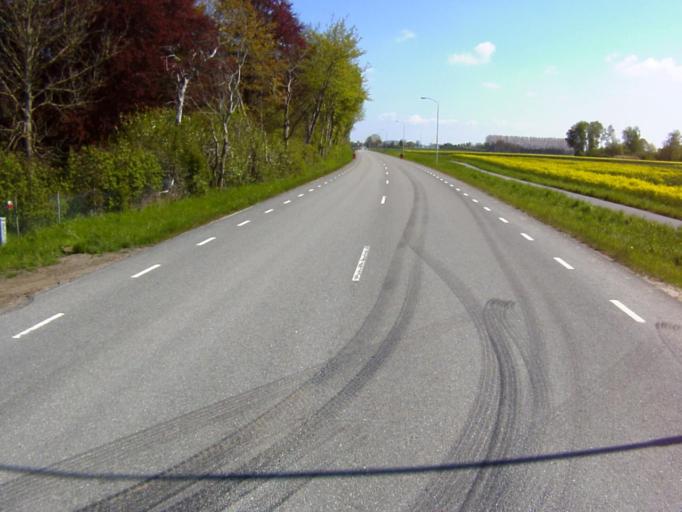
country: SE
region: Skane
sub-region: Kristianstads Kommun
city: Kristianstad
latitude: 56.0170
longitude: 14.1999
